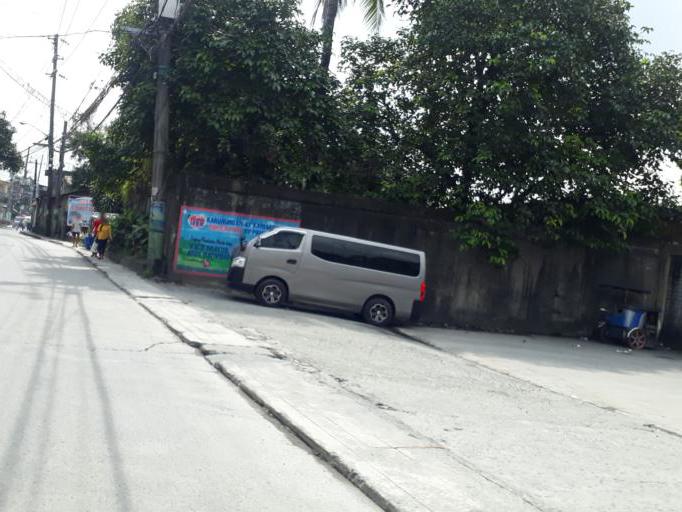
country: PH
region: Calabarzon
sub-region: Province of Rizal
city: Valenzuela
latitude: 14.7050
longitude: 121.0079
